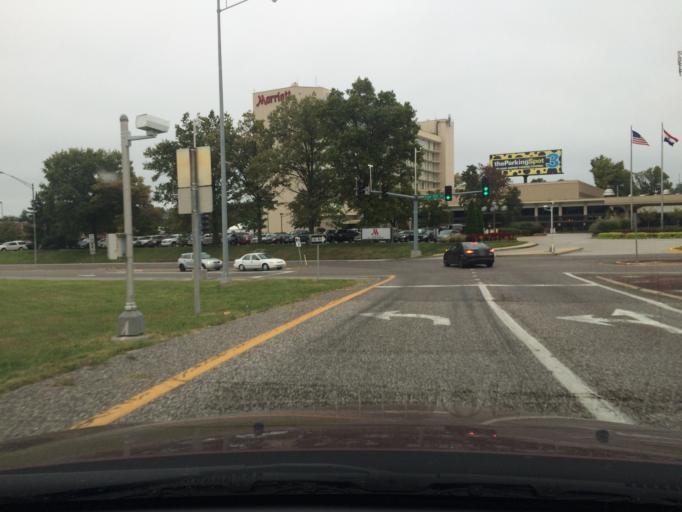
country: US
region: Missouri
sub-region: Saint Louis County
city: Woodson Terrace
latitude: 38.7390
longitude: -90.3686
